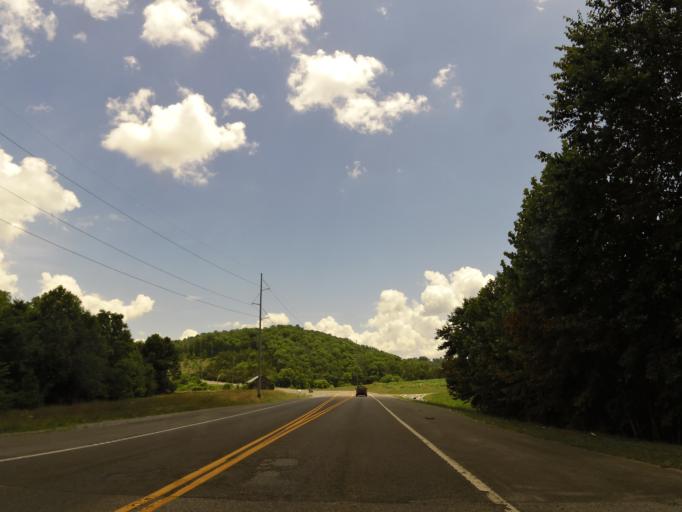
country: US
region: Tennessee
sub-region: Claiborne County
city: New Tazewell
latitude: 36.3966
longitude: -83.6860
